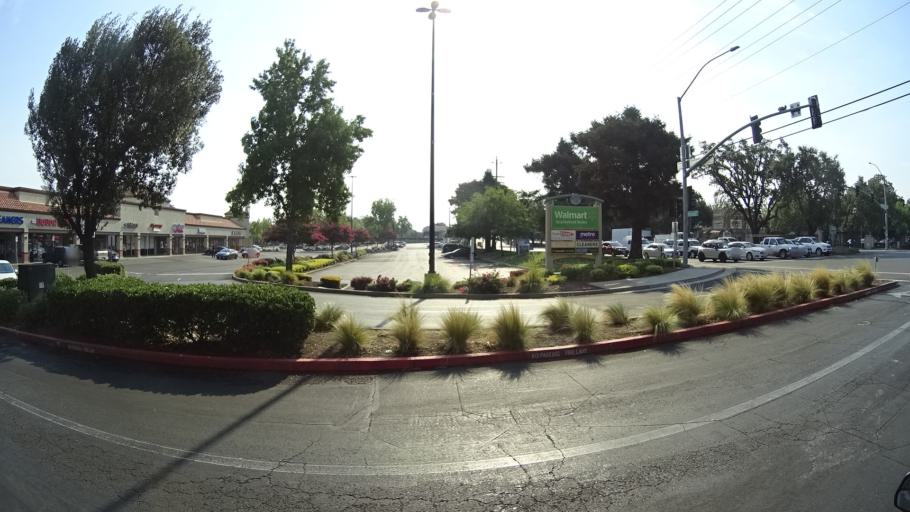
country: US
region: California
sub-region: Sacramento County
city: Elk Grove
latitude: 38.4094
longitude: -121.3926
